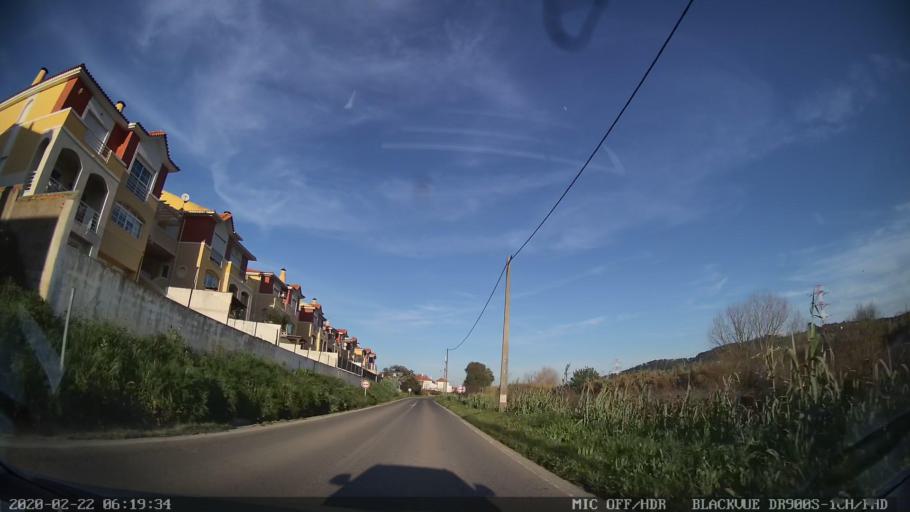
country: PT
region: Lisbon
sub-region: Vila Franca de Xira
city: Castanheira do Ribatejo
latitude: 39.0050
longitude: -8.9968
